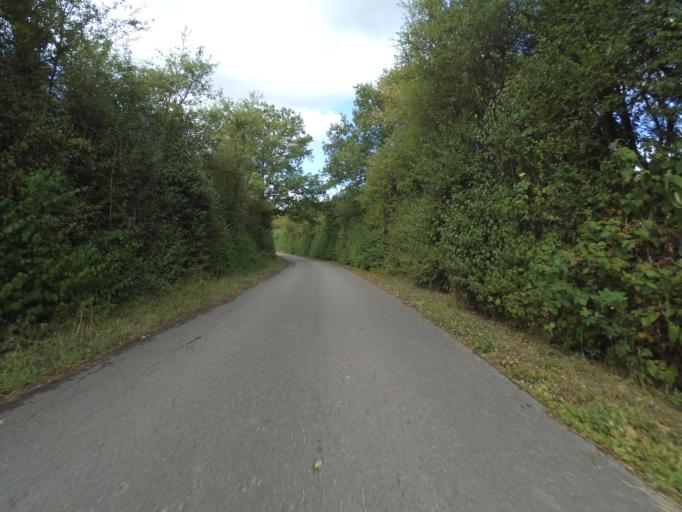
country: LU
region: Grevenmacher
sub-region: Canton de Remich
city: Lenningen
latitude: 49.6090
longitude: 6.3755
